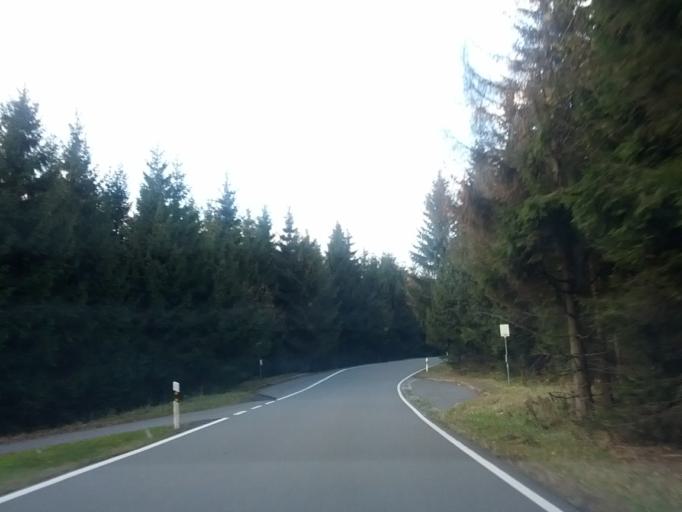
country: DE
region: Thuringia
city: Brotterode
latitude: 50.8397
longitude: 10.4059
